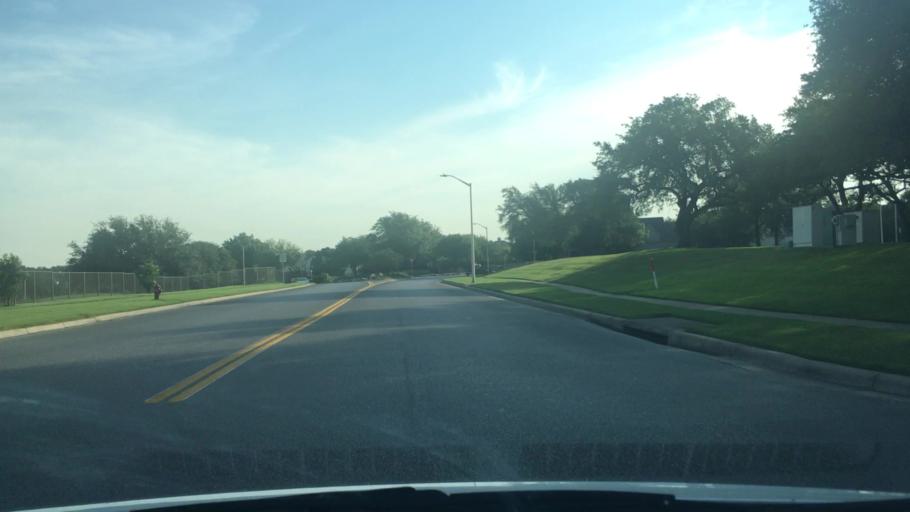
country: US
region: Texas
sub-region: Williamson County
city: Anderson Mill
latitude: 30.4667
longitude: -97.8501
